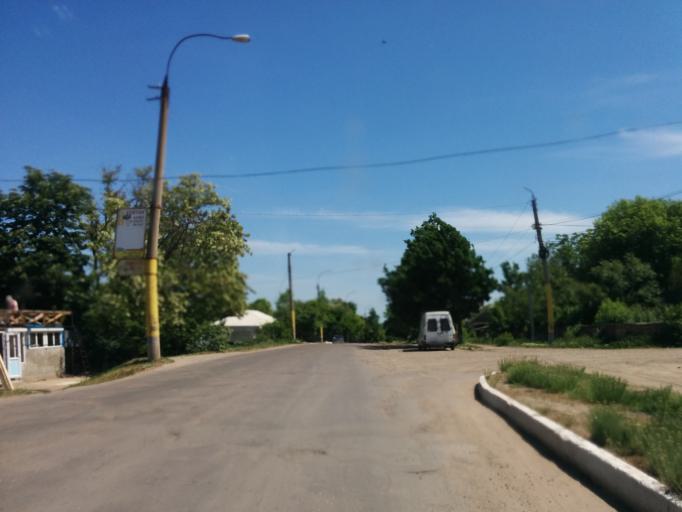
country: MD
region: Raionul Soroca
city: Soroca
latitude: 48.1623
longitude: 28.2813
